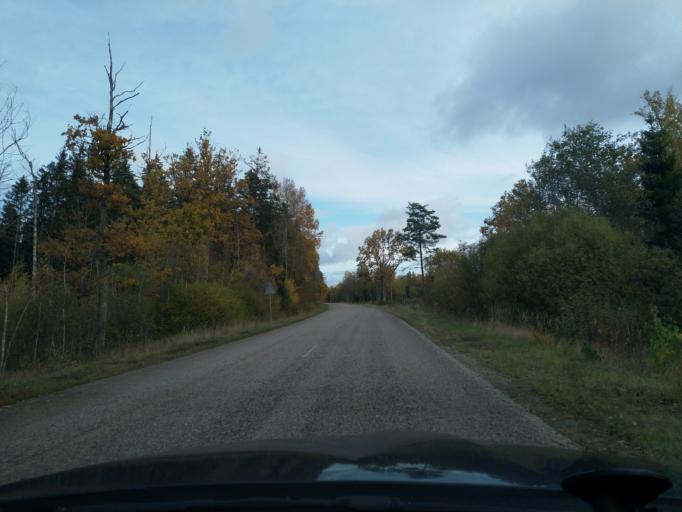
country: LV
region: Dundaga
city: Dundaga
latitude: 57.5440
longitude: 22.3503
